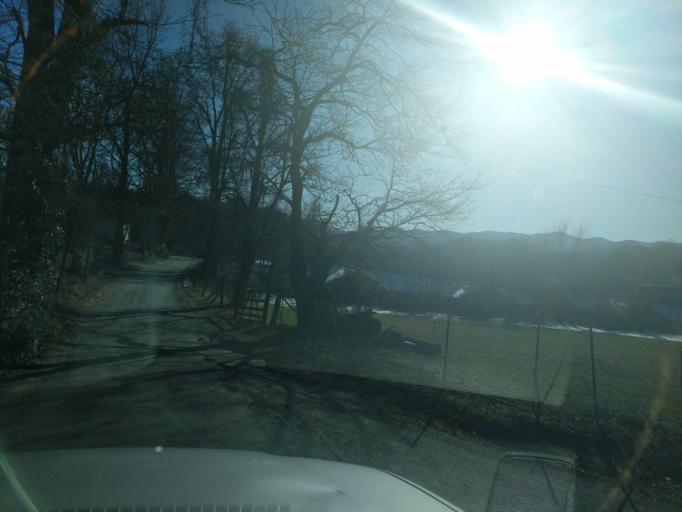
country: US
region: Georgia
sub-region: Towns County
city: Hiawassee
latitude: 34.9470
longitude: -83.7303
